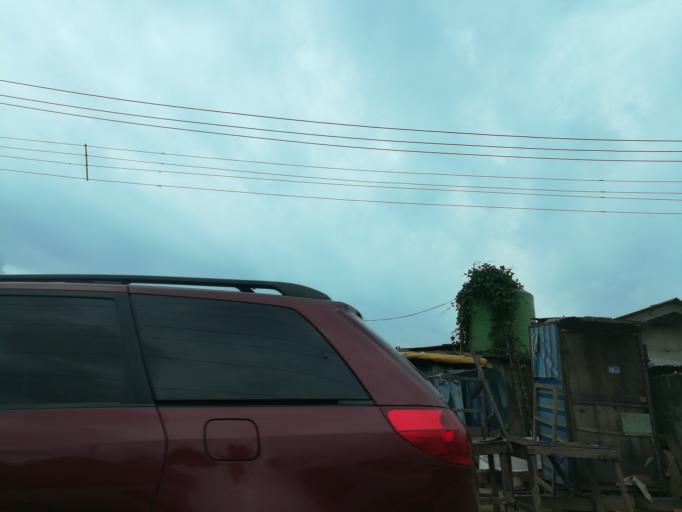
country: NG
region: Lagos
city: Ojota
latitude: 6.6187
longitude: 3.3969
